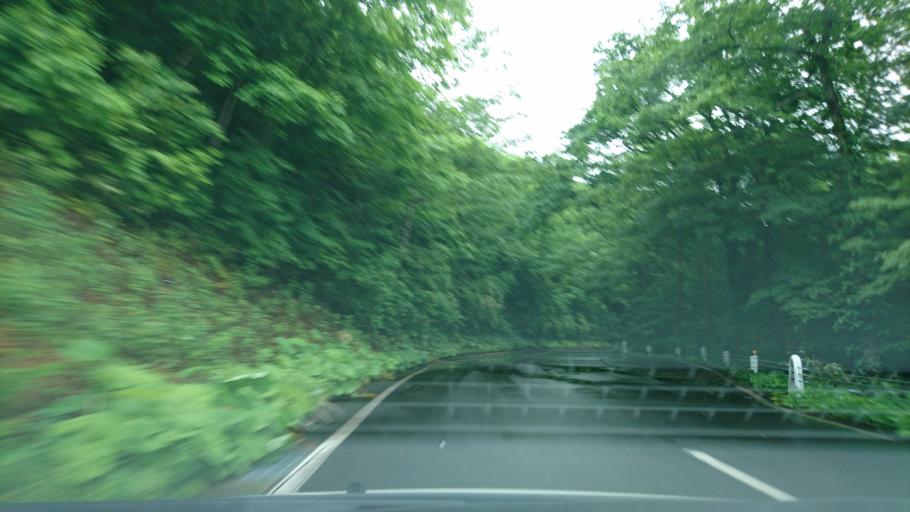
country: JP
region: Iwate
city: Ichinoseki
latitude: 39.0018
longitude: 140.8354
